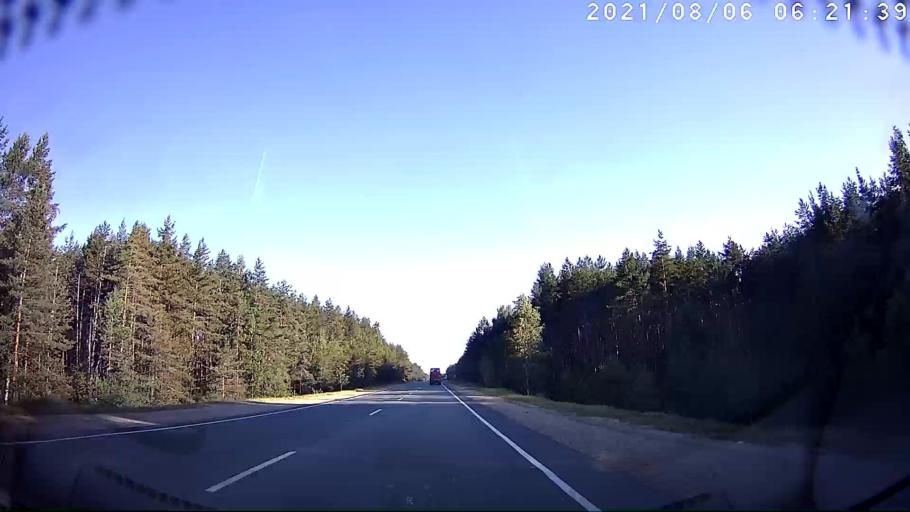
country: RU
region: Mariy-El
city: Krasnogorskiy
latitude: 56.0710
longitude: 48.3632
